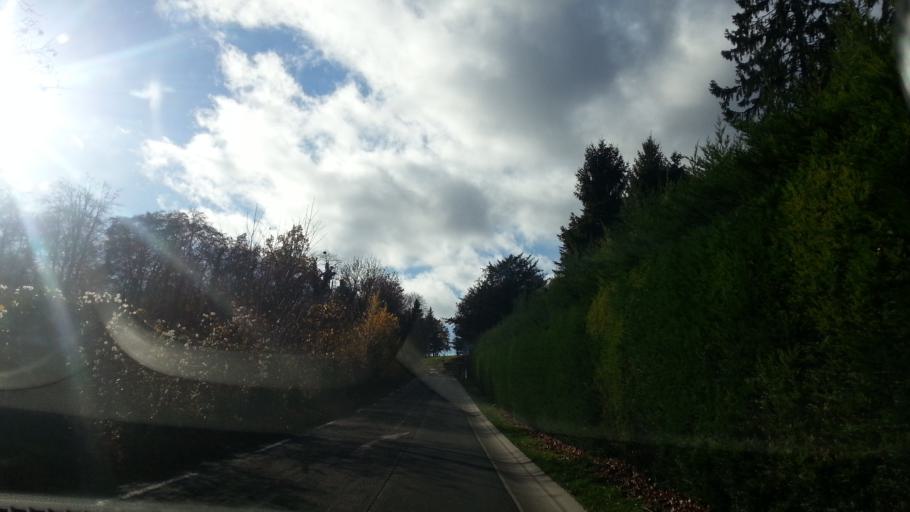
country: FR
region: Picardie
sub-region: Departement de l'Oise
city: Gouvieux
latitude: 49.1939
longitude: 2.4301
